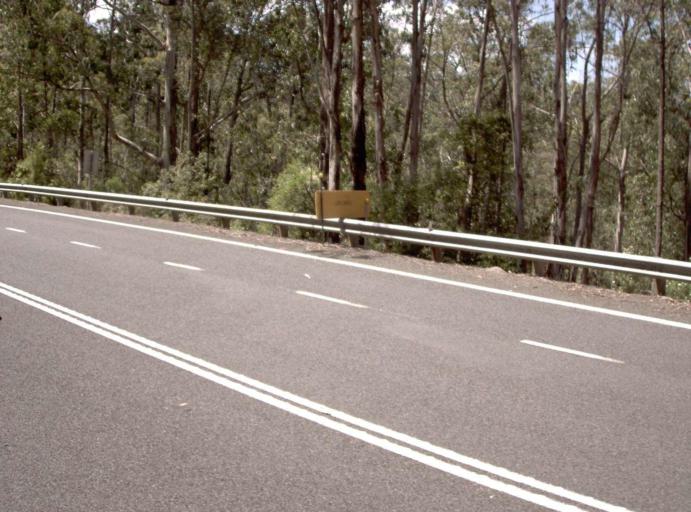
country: AU
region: New South Wales
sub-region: Bombala
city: Bombala
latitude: -37.6186
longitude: 148.8916
